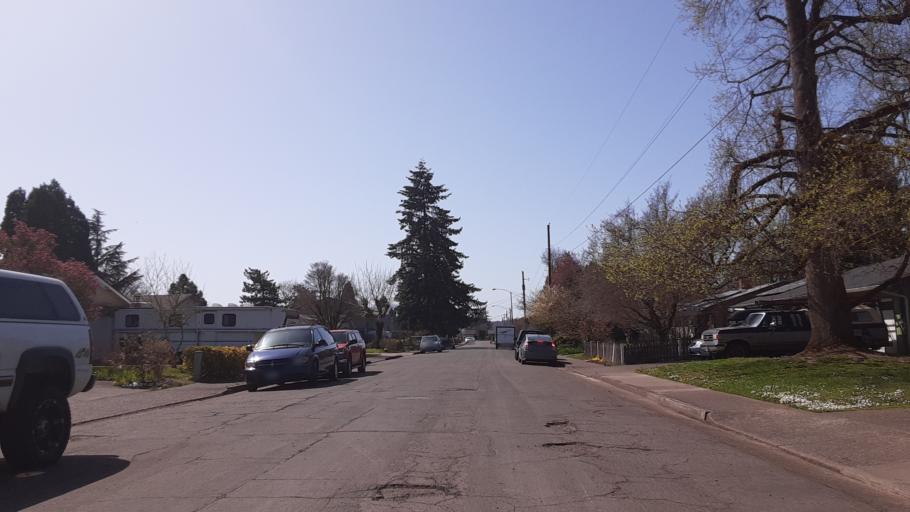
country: US
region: Oregon
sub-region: Benton County
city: Corvallis
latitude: 44.5397
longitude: -123.2566
